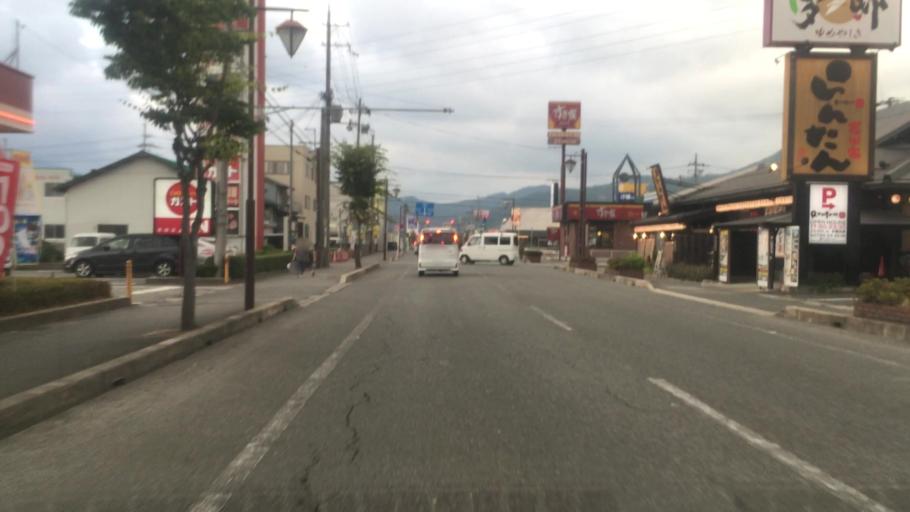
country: JP
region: Hyogo
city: Toyooka
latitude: 35.5527
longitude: 134.8155
